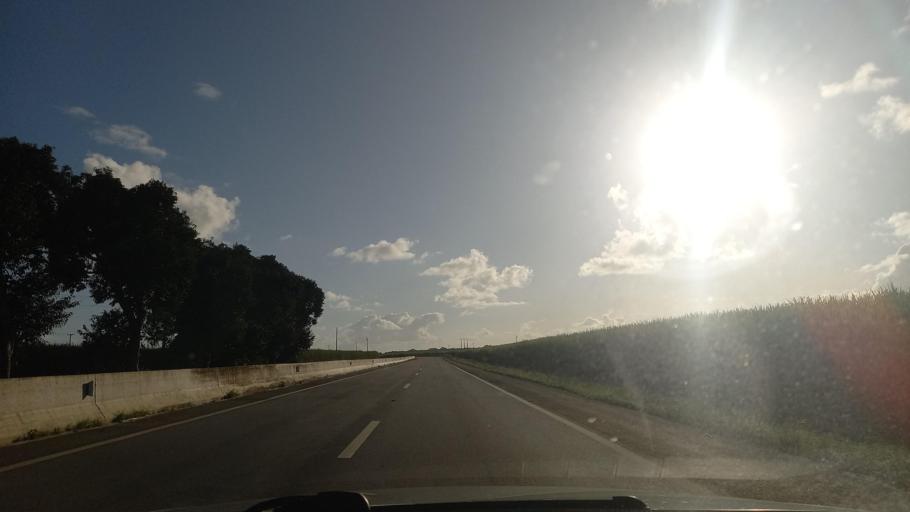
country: BR
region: Alagoas
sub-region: Sao Miguel Dos Campos
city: Sao Miguel dos Campos
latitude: -9.8008
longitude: -36.1899
